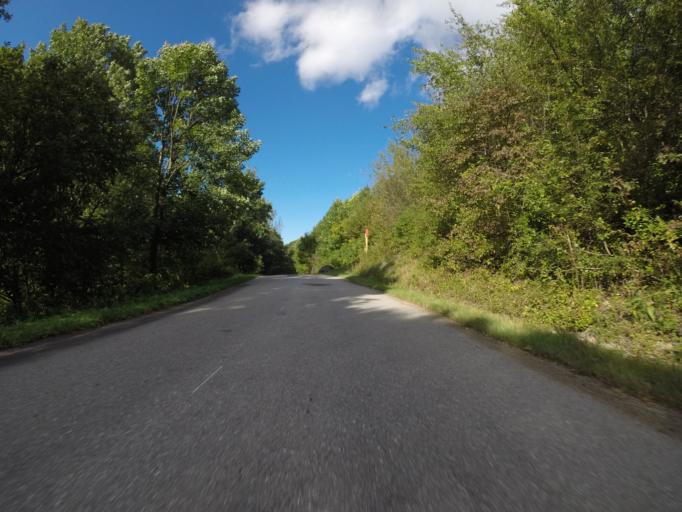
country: SK
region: Nitriansky
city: Ilava
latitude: 48.9727
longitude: 18.3816
